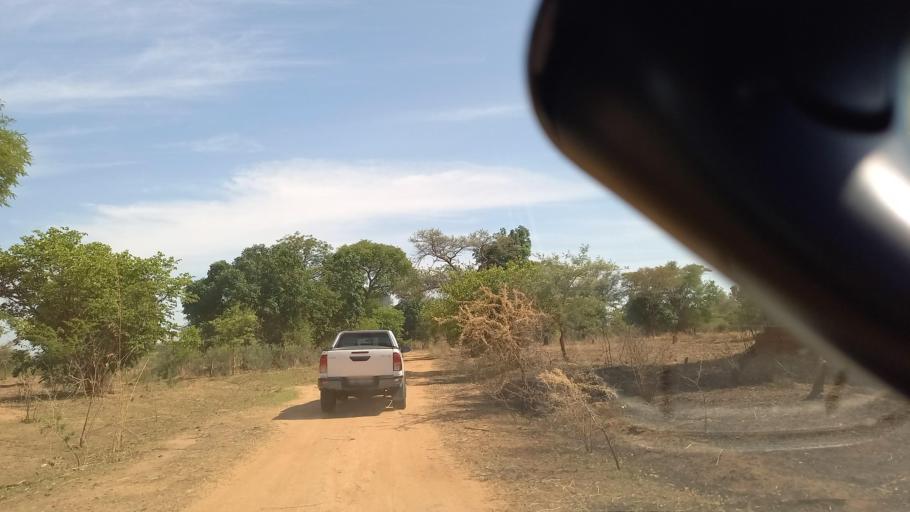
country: ZM
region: Southern
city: Mazabuka
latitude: -16.0337
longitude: 27.6234
